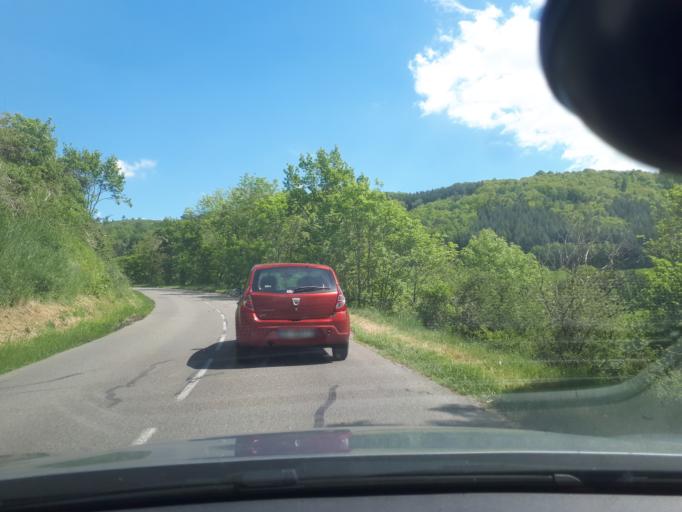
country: FR
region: Rhone-Alpes
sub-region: Departement du Rhone
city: Aveize
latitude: 45.6903
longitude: 4.5052
